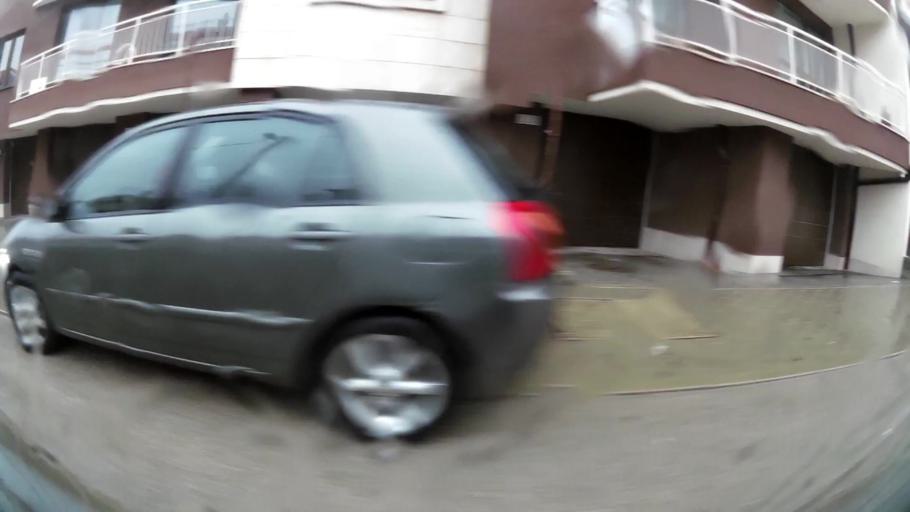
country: BG
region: Sofia-Capital
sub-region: Stolichna Obshtina
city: Sofia
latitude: 42.6434
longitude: 23.3315
